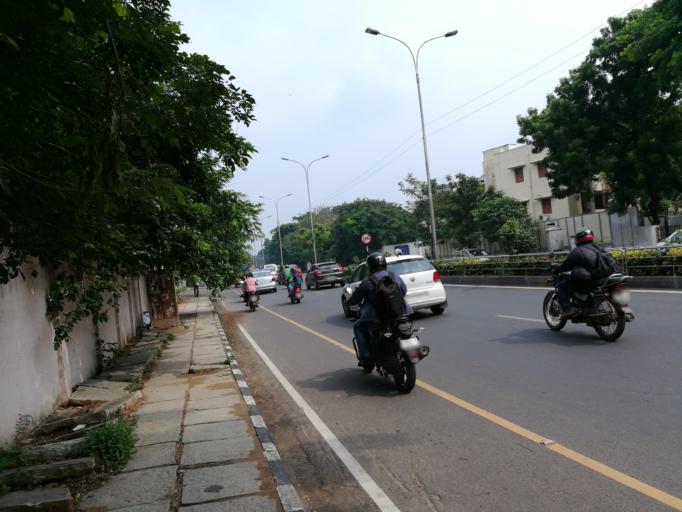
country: IN
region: Tamil Nadu
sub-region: Chennai
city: Gandhi Nagar
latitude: 13.0151
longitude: 80.2405
